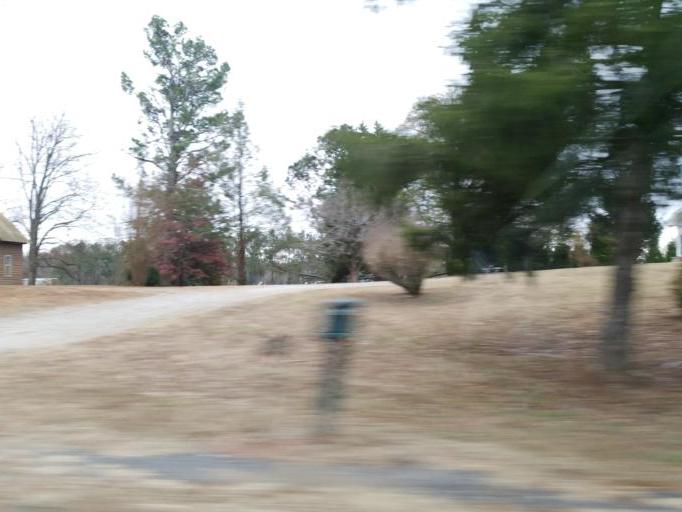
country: US
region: Georgia
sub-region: Dawson County
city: Dawsonville
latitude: 34.4847
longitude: -84.1682
